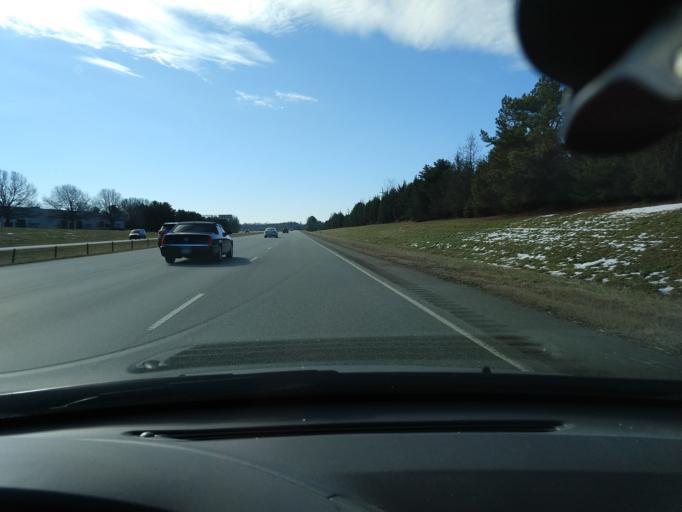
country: US
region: North Carolina
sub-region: Guilford County
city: Oak Ridge
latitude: 36.1036
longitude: -79.9656
